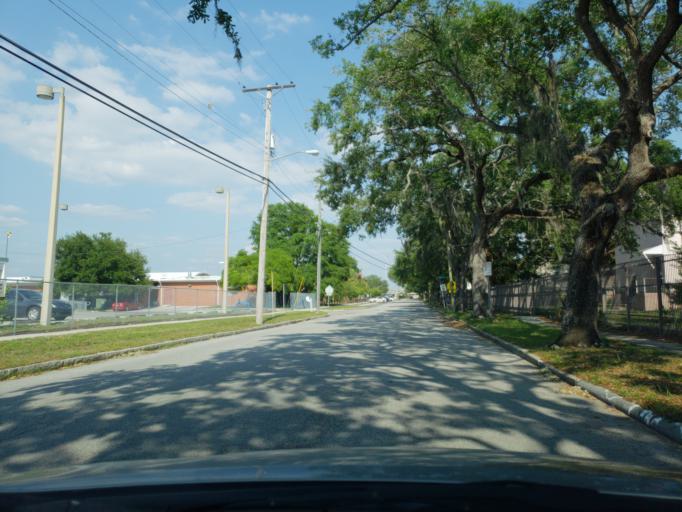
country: US
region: Florida
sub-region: Hillsborough County
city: Tampa
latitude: 27.9593
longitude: -82.4731
